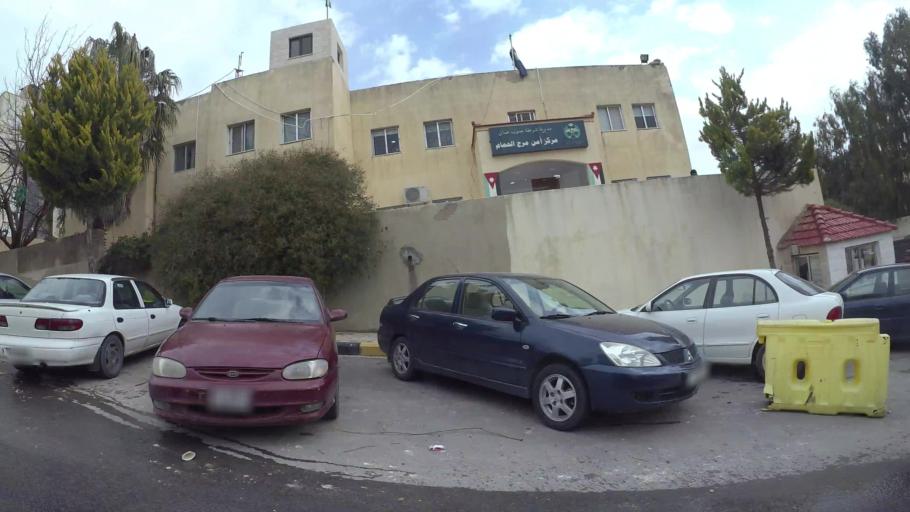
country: JO
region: Amman
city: Umm as Summaq
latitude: 31.9030
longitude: 35.8383
